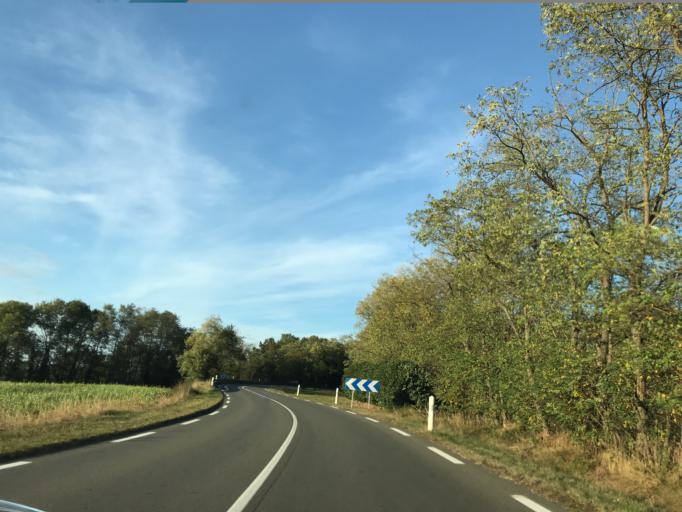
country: FR
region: Auvergne
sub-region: Departement du Puy-de-Dome
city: Puy-Guillaume
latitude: 45.9851
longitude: 3.4854
